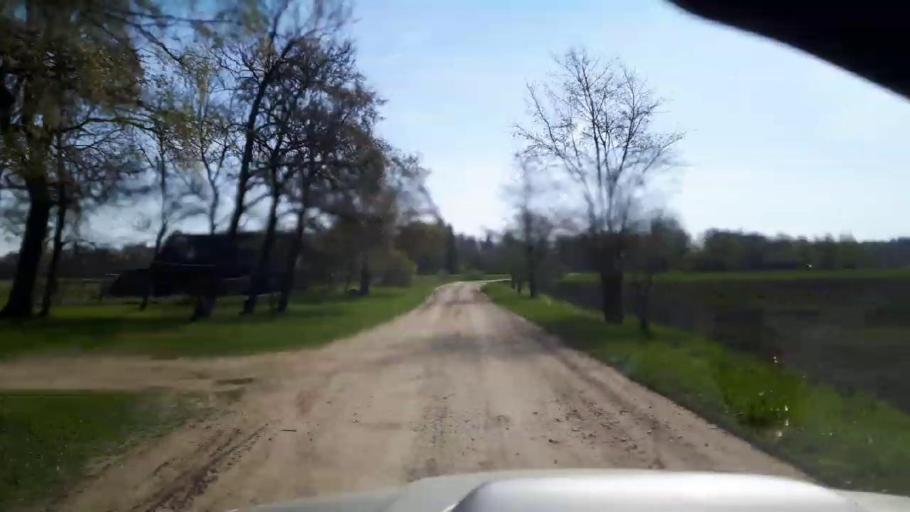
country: EE
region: Paernumaa
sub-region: Tootsi vald
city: Tootsi
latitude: 58.4851
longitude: 24.9000
